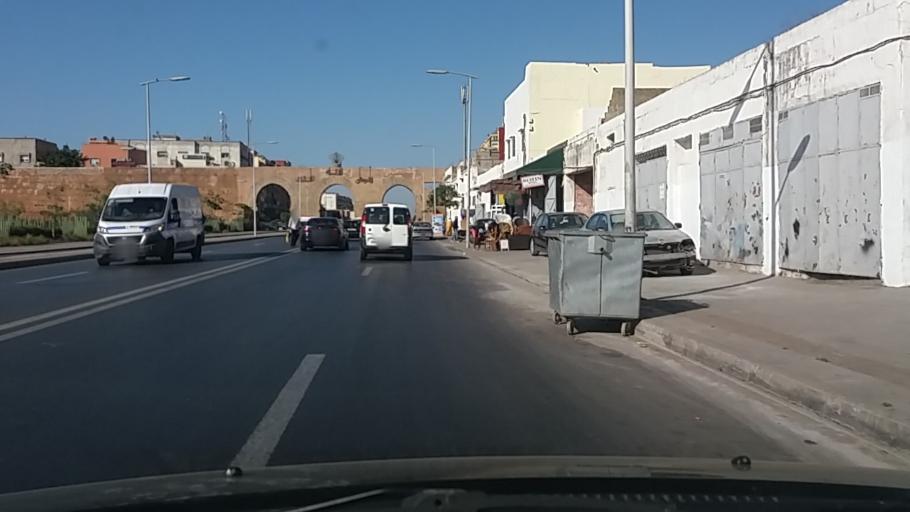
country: MA
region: Rabat-Sale-Zemmour-Zaer
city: Sale
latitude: 34.0469
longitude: -6.8170
